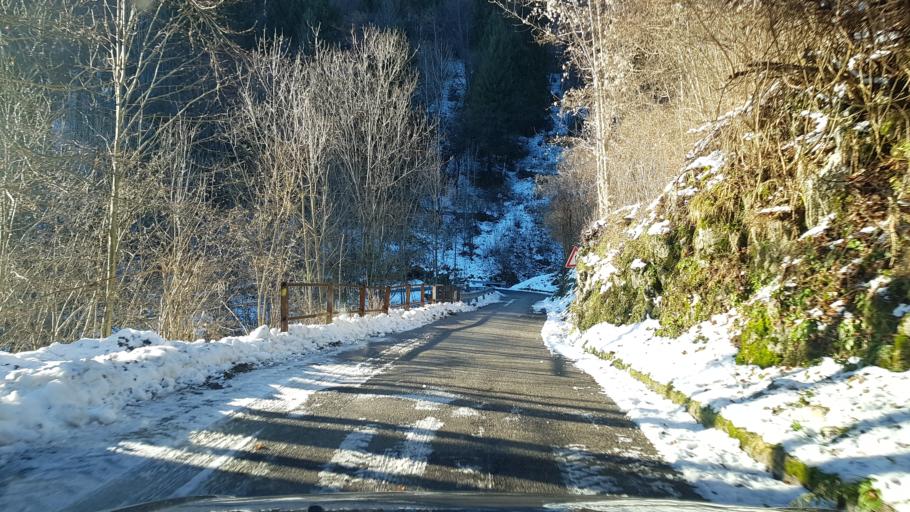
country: IT
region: Friuli Venezia Giulia
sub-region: Provincia di Udine
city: Savogna
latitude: 46.1932
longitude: 13.5272
